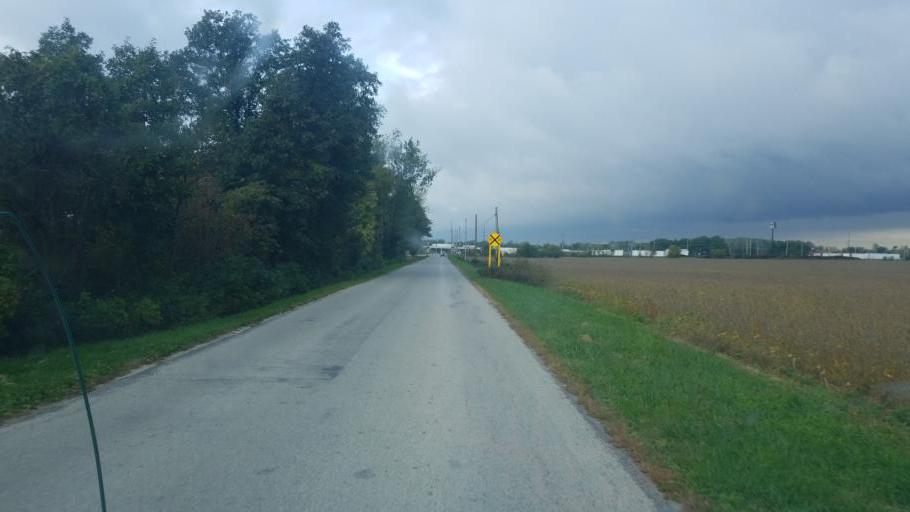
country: US
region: Ohio
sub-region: Wood County
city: North Baltimore
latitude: 41.1822
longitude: -83.6416
